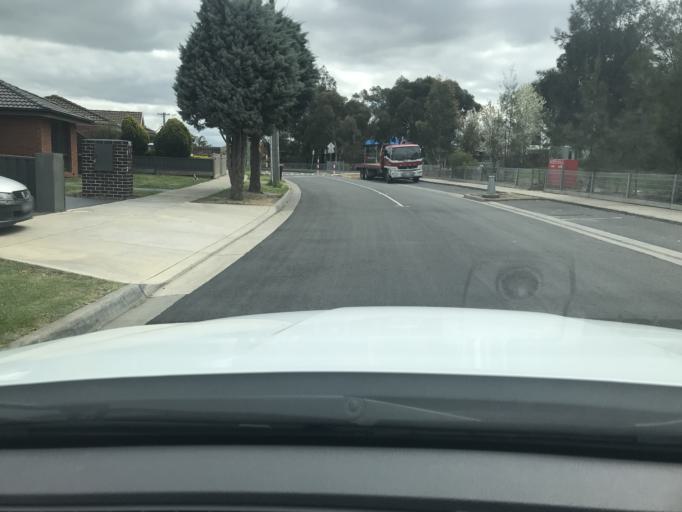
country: AU
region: Victoria
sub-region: Hume
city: Craigieburn
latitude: -37.5920
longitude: 144.9220
